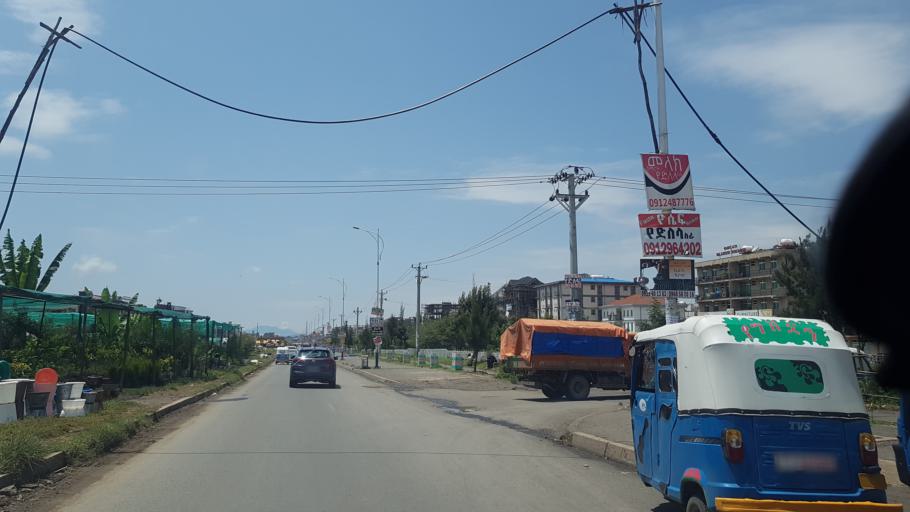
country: ET
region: Adis Abeba
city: Addis Ababa
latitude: 9.0187
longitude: 38.8521
